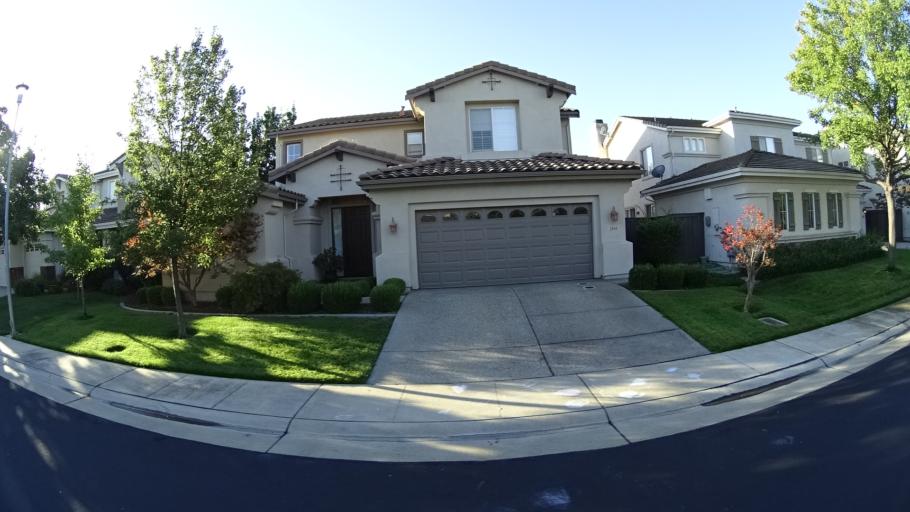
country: US
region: California
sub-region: Sacramento County
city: Laguna
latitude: 38.3962
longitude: -121.4758
